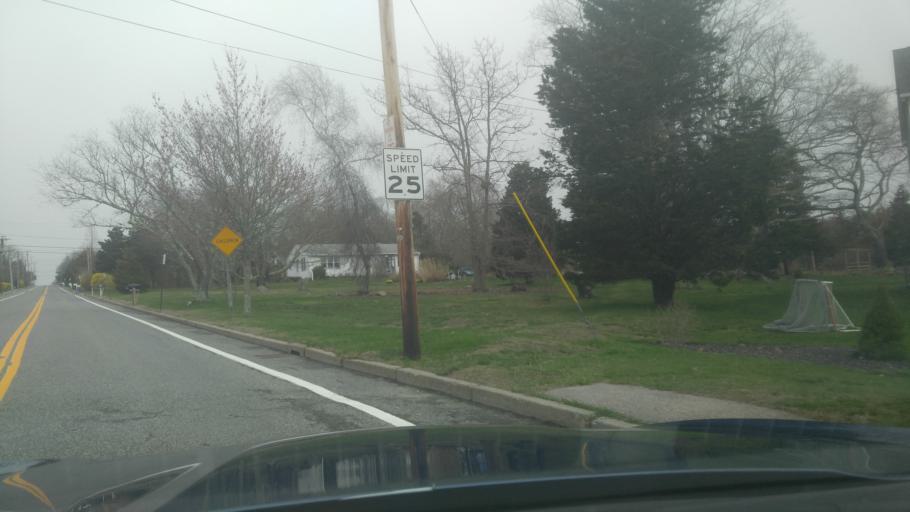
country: US
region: Rhode Island
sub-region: Newport County
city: Jamestown
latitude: 41.4890
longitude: -71.3799
